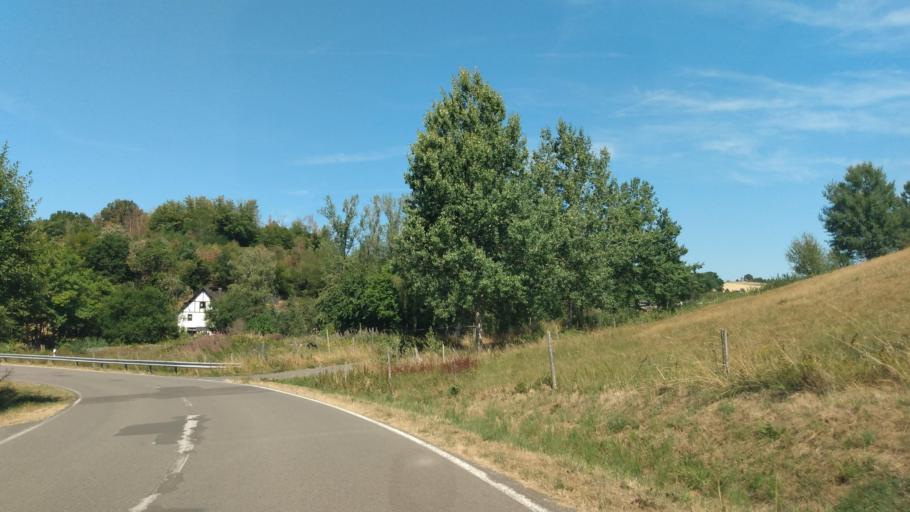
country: DE
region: Rheinland-Pfalz
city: Morbach
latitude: 49.8331
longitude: 7.0805
